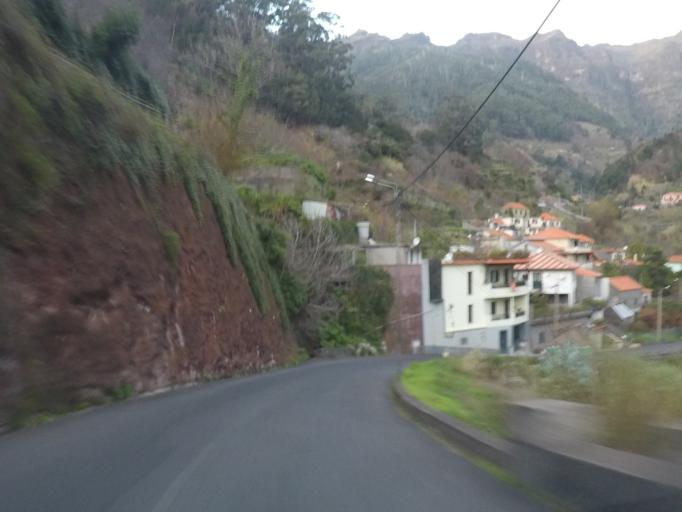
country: PT
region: Madeira
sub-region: Camara de Lobos
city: Curral das Freiras
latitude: 32.7347
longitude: -16.9700
